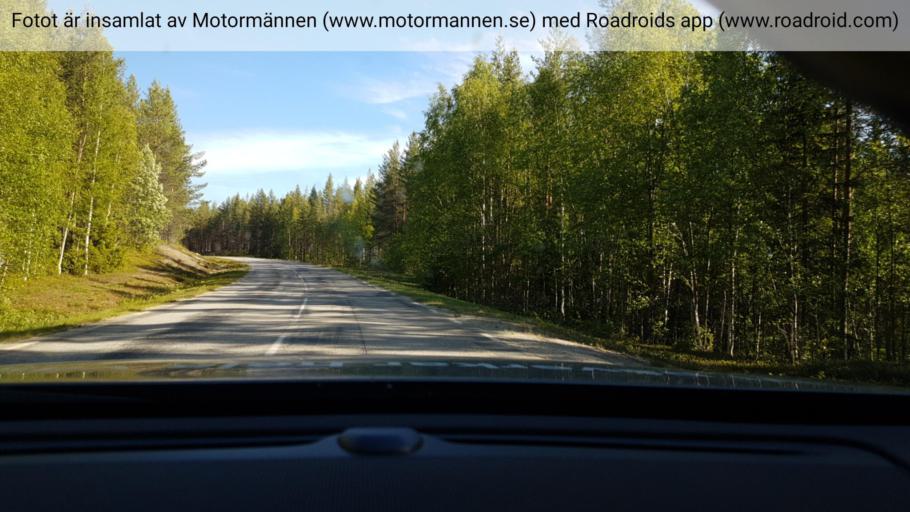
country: SE
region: Vaesterbotten
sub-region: Lycksele Kommun
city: Lycksele
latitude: 64.7991
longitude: 18.9553
